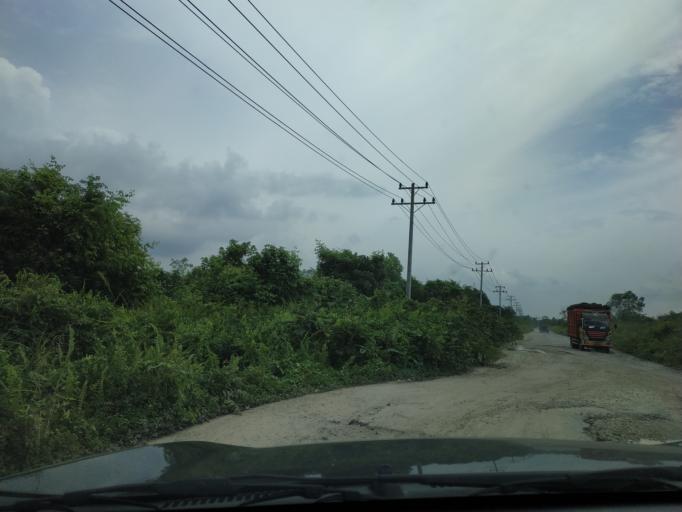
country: ID
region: Riau
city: Siak Sri Indrapura
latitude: 0.9116
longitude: 102.3044
